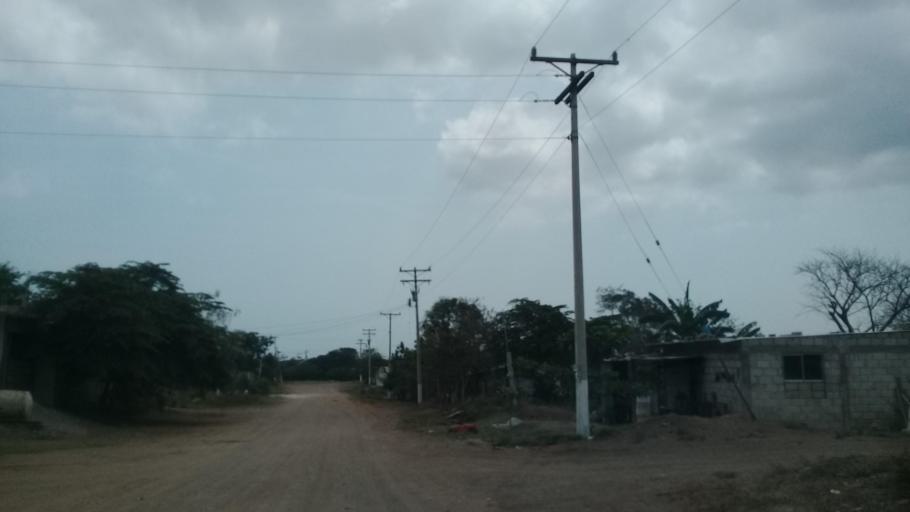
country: MX
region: Veracruz
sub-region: Veracruz
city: Las Amapolas
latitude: 19.1350
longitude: -96.2408
